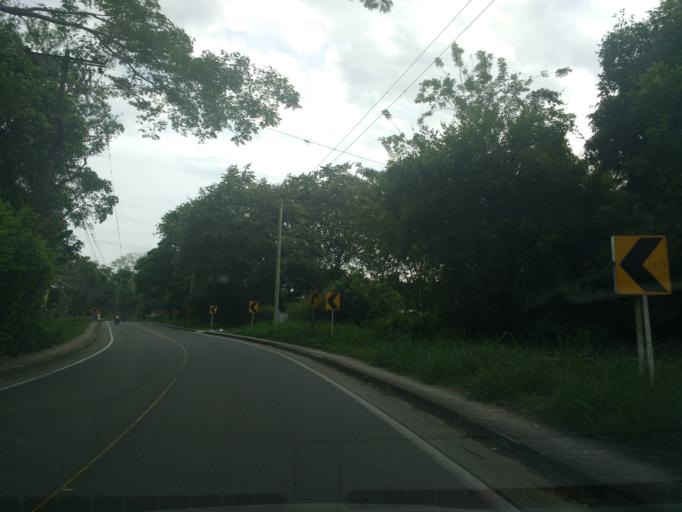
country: CO
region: Cauca
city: Miranda
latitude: 3.2790
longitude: -76.2218
